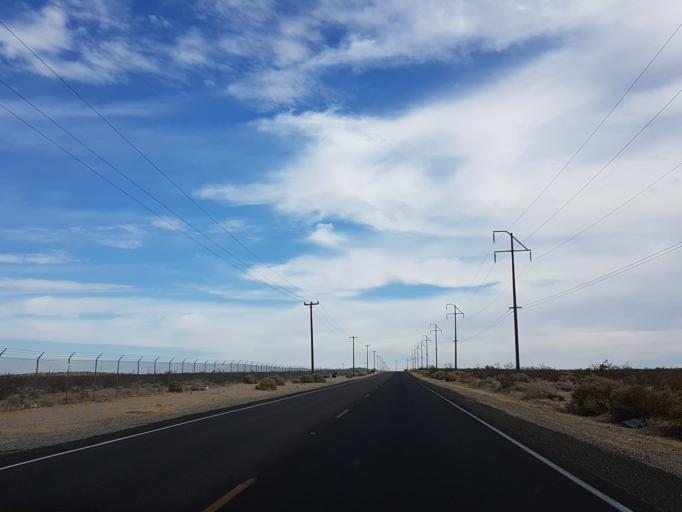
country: US
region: California
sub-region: Kern County
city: Ridgecrest
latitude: 35.6226
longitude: -117.6080
